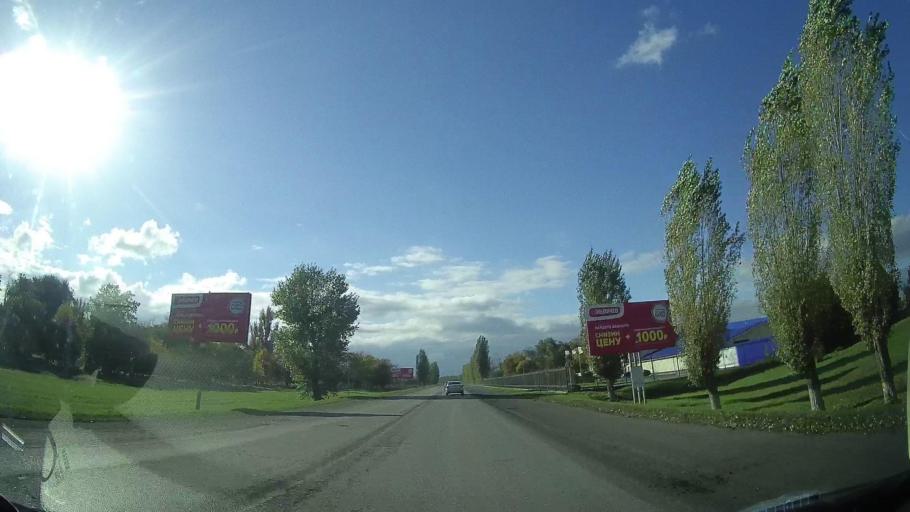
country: RU
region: Rostov
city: Tselina
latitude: 46.5322
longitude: 41.0020
